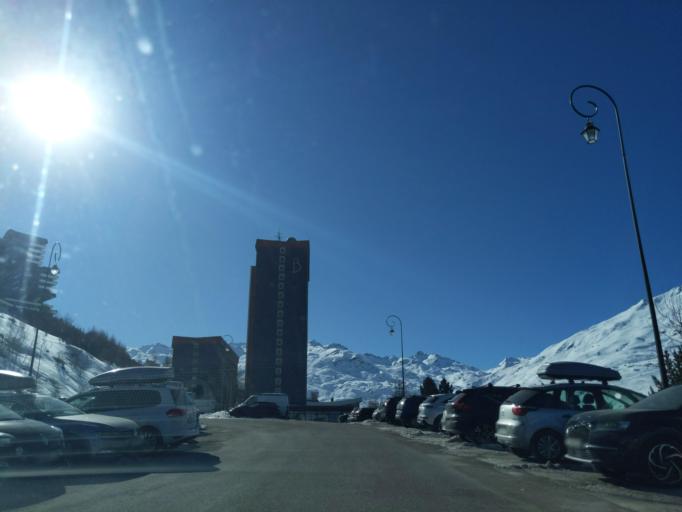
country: FR
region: Rhone-Alpes
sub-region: Departement de la Savoie
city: Val Thorens
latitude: 45.3285
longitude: 6.5378
